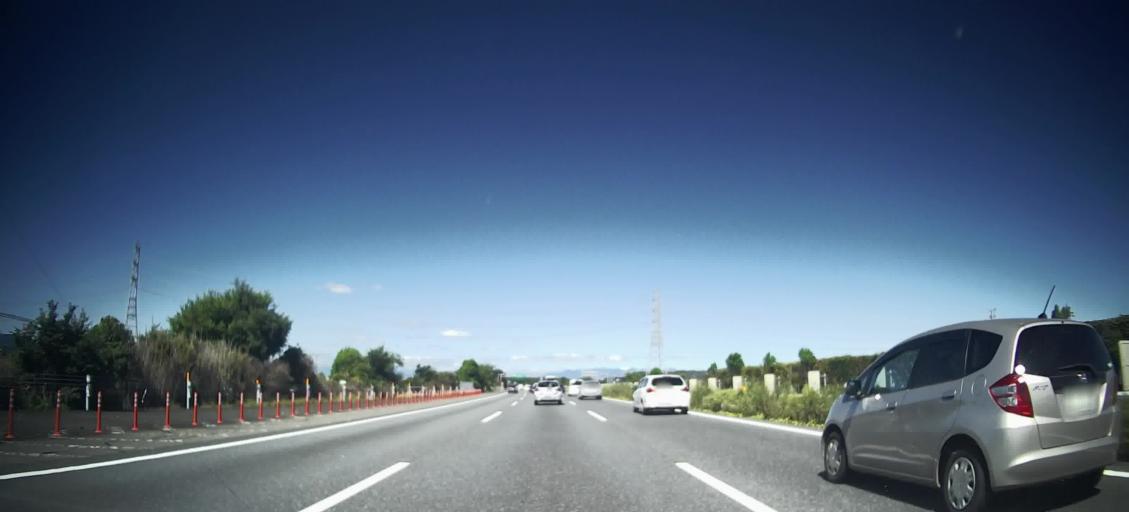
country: JP
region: Saitama
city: Honjo
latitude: 36.1998
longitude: 139.1823
